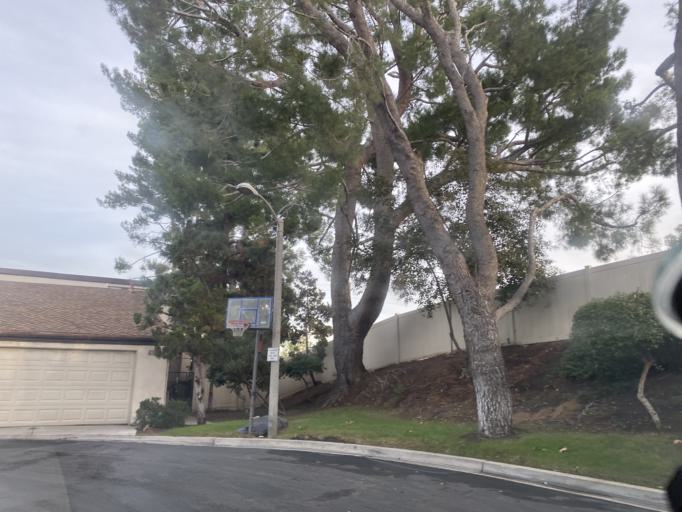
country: US
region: California
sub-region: Orange County
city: Brea
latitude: 33.8994
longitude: -117.8836
